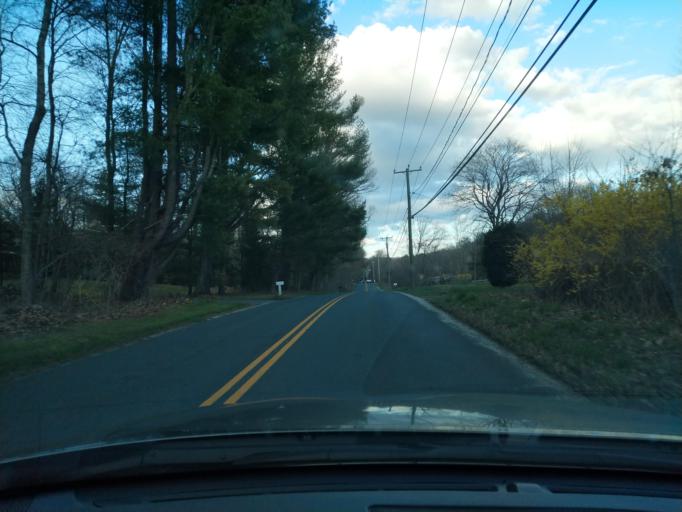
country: US
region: Connecticut
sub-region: Fairfield County
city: Newtown
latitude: 41.3603
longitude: -73.2739
